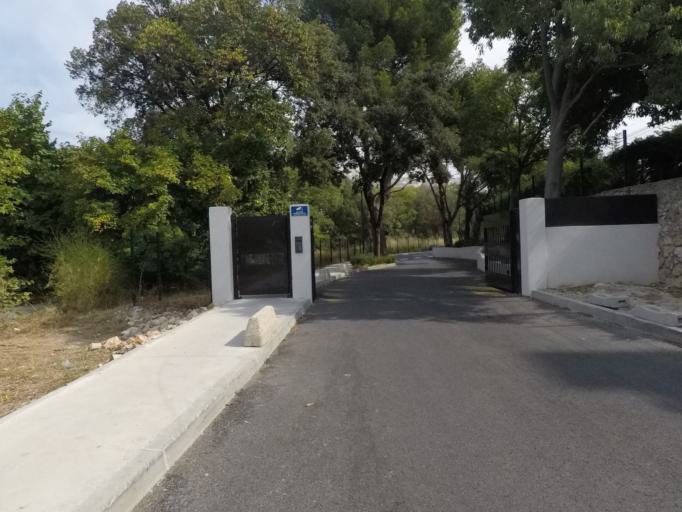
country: FR
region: Provence-Alpes-Cote d'Azur
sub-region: Departement des Bouches-du-Rhone
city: Marseille 09
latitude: 43.2558
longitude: 5.4209
